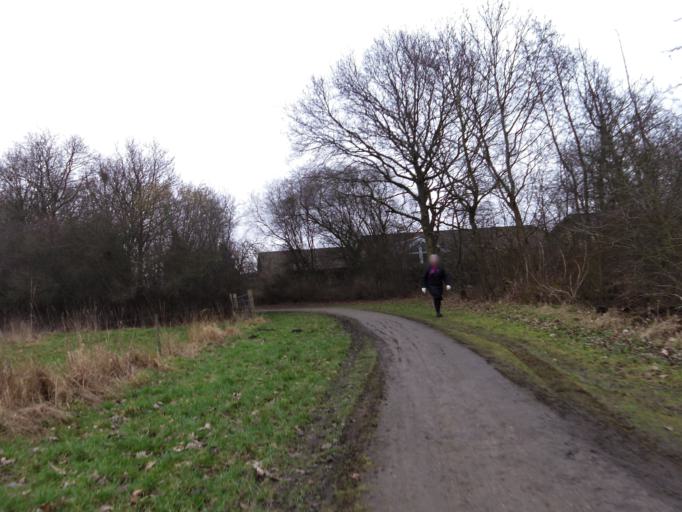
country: DK
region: South Denmark
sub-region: Odense Kommune
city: Neder Holluf
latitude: 55.3795
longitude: 10.4413
